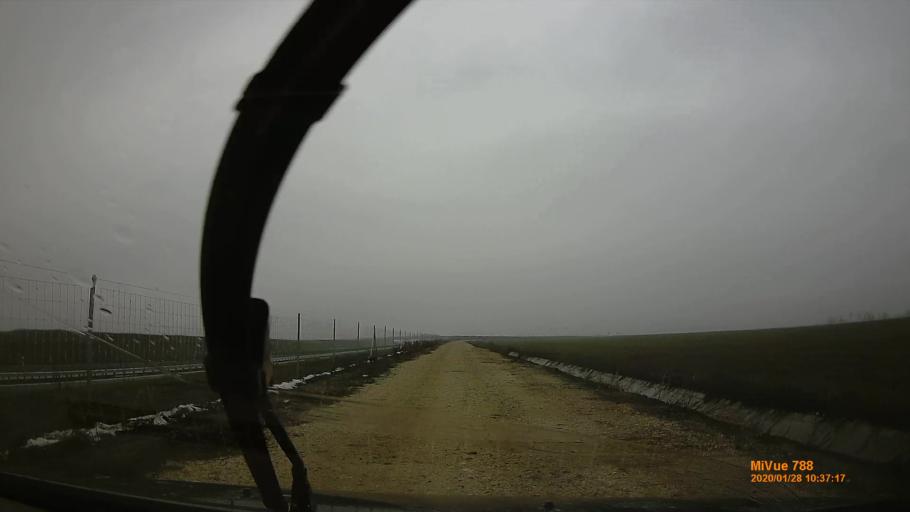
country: HU
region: Pest
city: Monor
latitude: 47.3551
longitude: 19.4888
